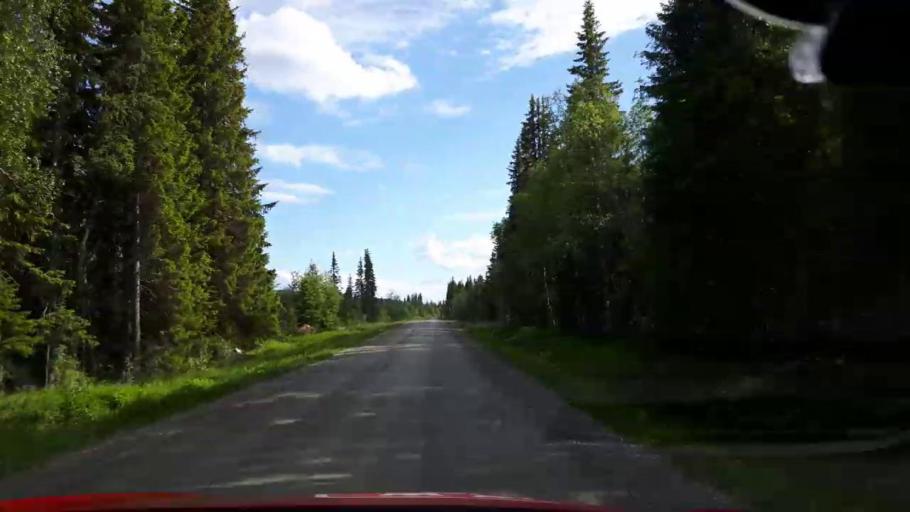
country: SE
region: Jaemtland
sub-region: Krokoms Kommun
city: Valla
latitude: 63.8127
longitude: 14.0492
